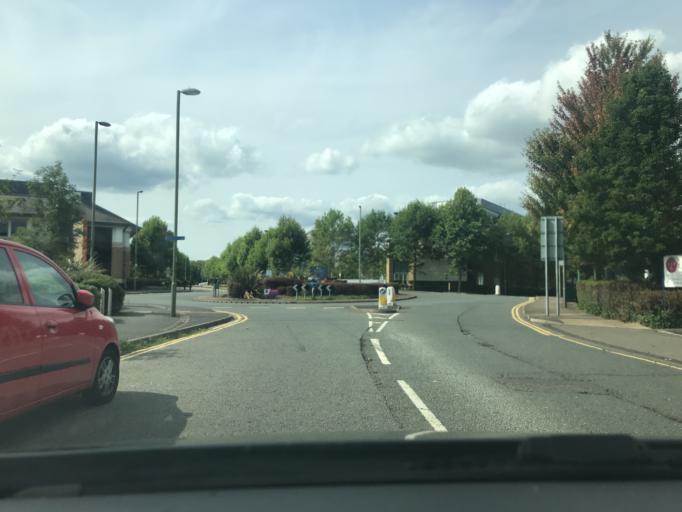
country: GB
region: England
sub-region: Surrey
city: Addlestone
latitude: 51.3720
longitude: -0.4741
